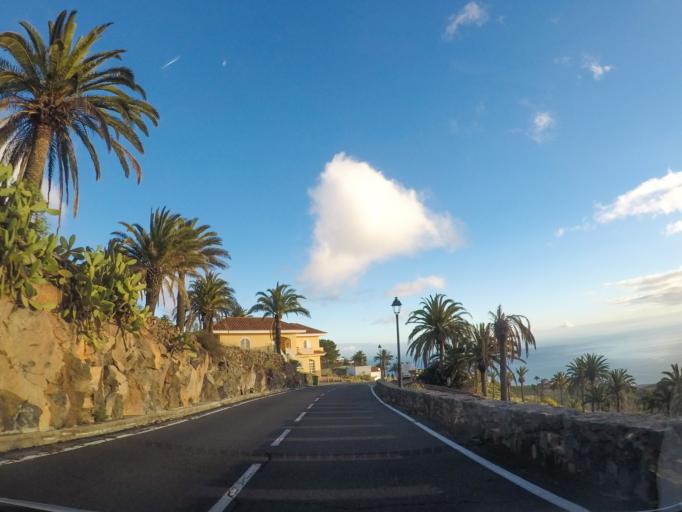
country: ES
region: Canary Islands
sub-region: Provincia de Santa Cruz de Tenerife
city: Alajero
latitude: 28.0596
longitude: -17.2351
